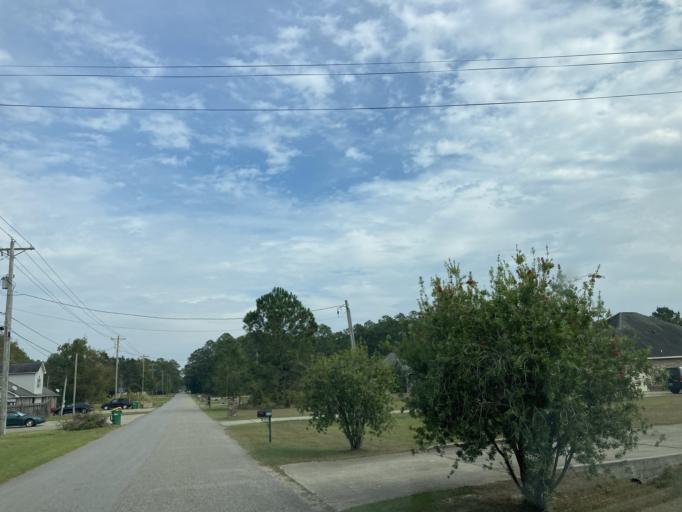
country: US
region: Mississippi
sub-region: Jackson County
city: Saint Martin
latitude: 30.4704
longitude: -88.8448
